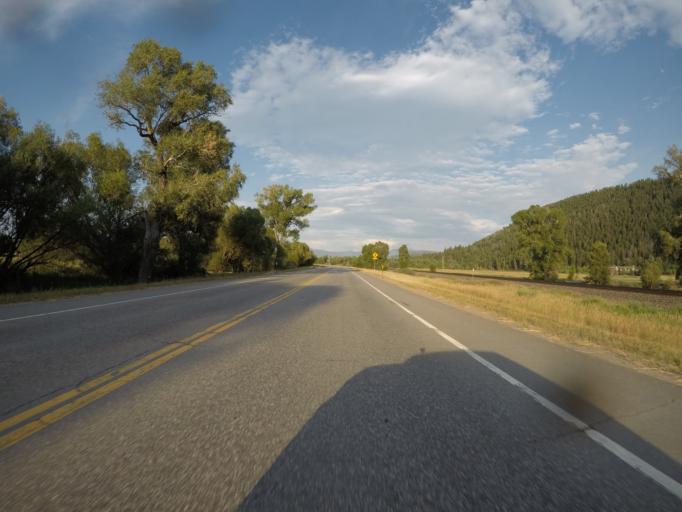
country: US
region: Colorado
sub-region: Routt County
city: Steamboat Springs
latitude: 40.4841
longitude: -106.9801
